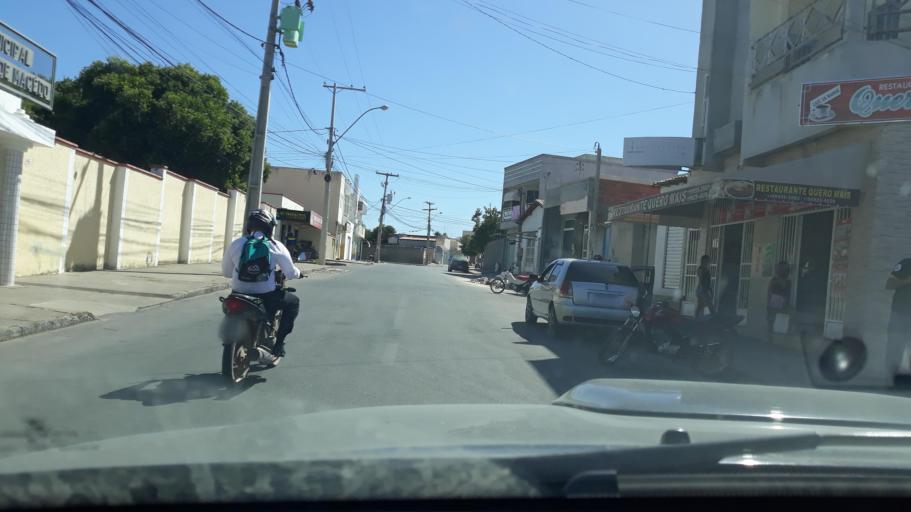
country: BR
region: Bahia
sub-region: Guanambi
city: Guanambi
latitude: -14.2193
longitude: -42.7953
